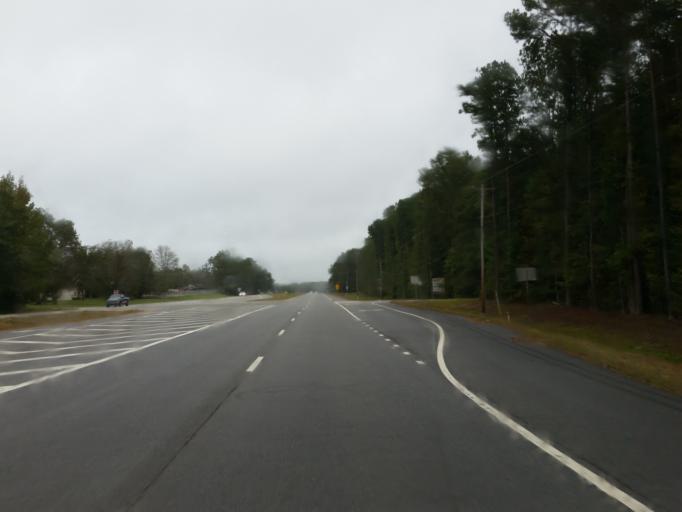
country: US
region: Georgia
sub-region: Lamar County
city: Barnesville
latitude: 33.1057
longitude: -84.1926
